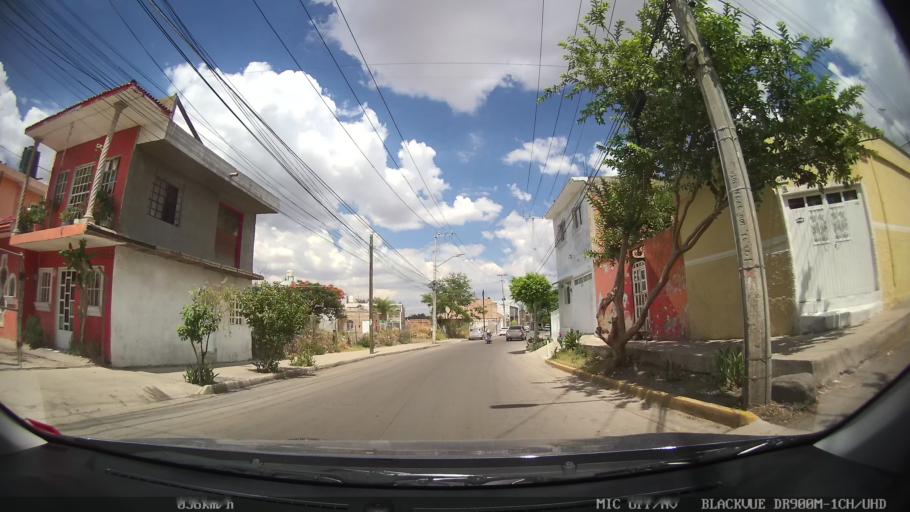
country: MX
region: Jalisco
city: Tlaquepaque
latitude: 20.6587
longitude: -103.2730
